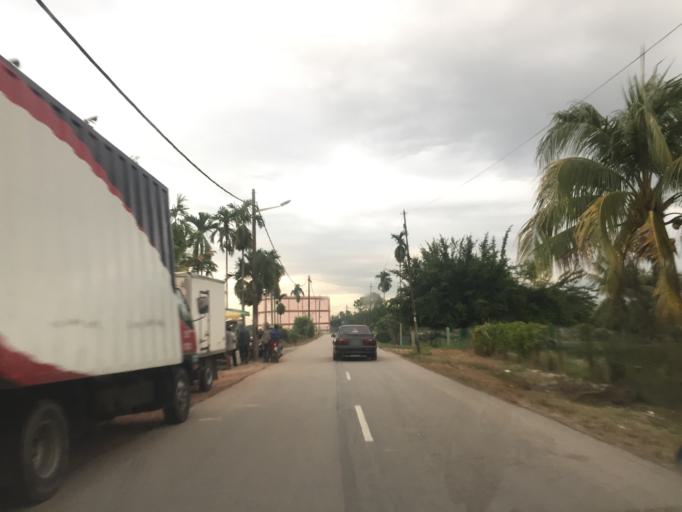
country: MY
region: Penang
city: Tasek Glugor
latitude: 5.5391
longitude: 100.5214
